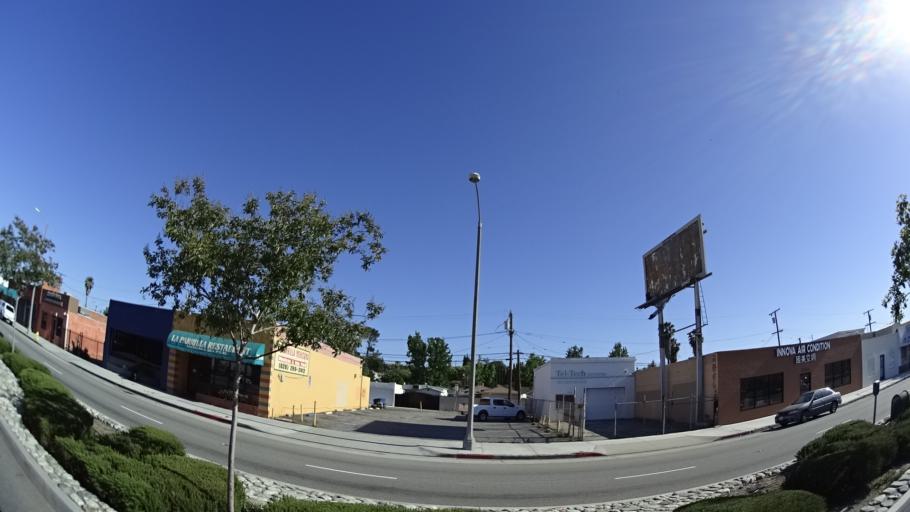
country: US
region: California
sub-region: Los Angeles County
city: Alhambra
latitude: 34.0766
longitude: -118.1569
